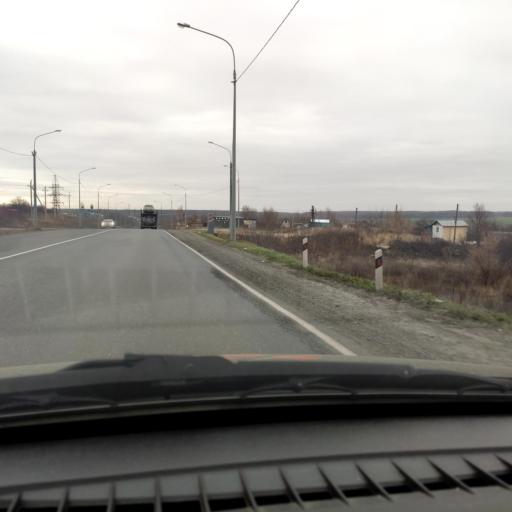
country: RU
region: Samara
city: Zhigulevsk
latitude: 53.3705
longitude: 49.4570
